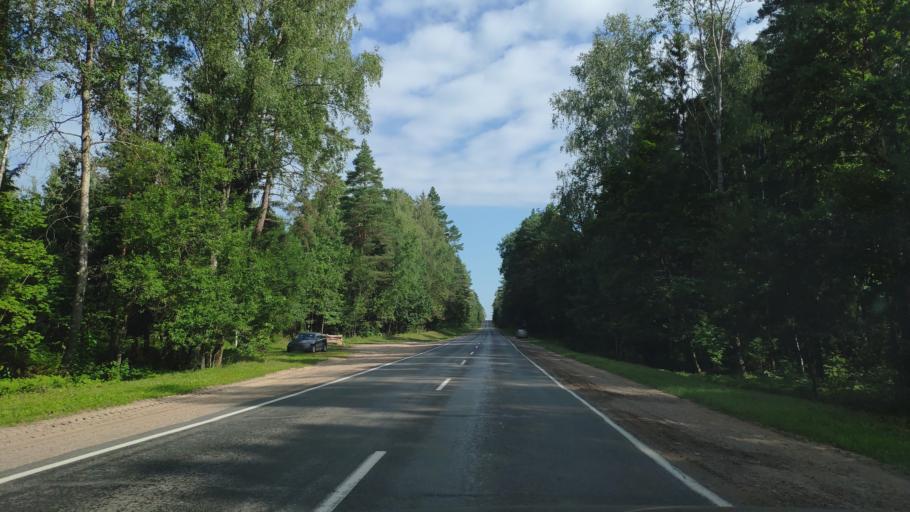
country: BY
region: Minsk
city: Novosel'ye
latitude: 53.9358
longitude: 27.2439
